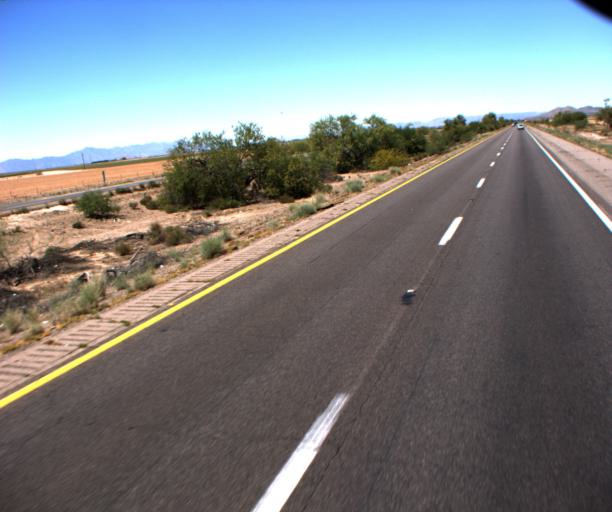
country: US
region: Arizona
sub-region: Pinal County
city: Sacaton
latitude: 33.0787
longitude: -111.8116
